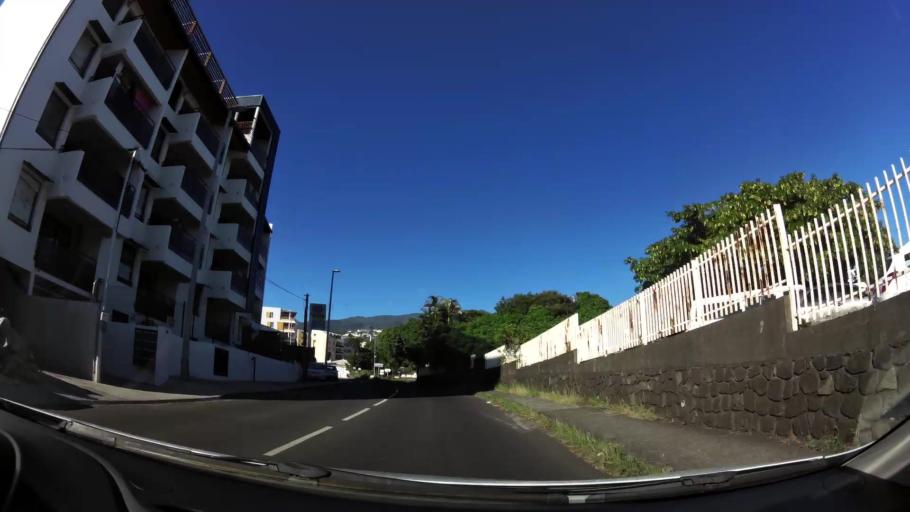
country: RE
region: Reunion
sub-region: Reunion
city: Saint-Denis
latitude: -20.8986
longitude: 55.4752
